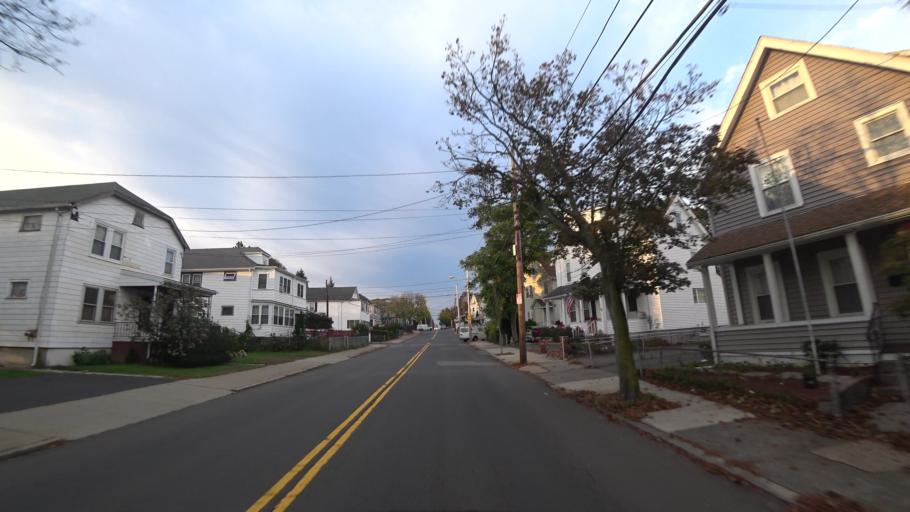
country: US
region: Massachusetts
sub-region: Middlesex County
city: Everett
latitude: 42.4234
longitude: -71.0411
